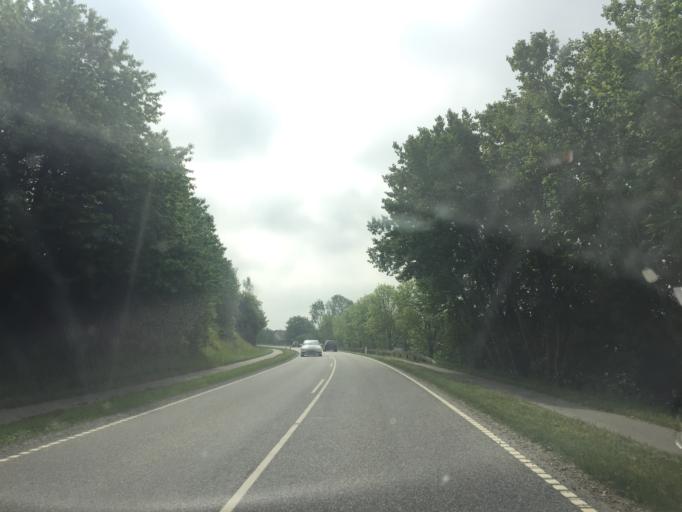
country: DK
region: South Denmark
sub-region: Kolding Kommune
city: Sonder Bjert
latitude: 55.4627
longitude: 9.5360
